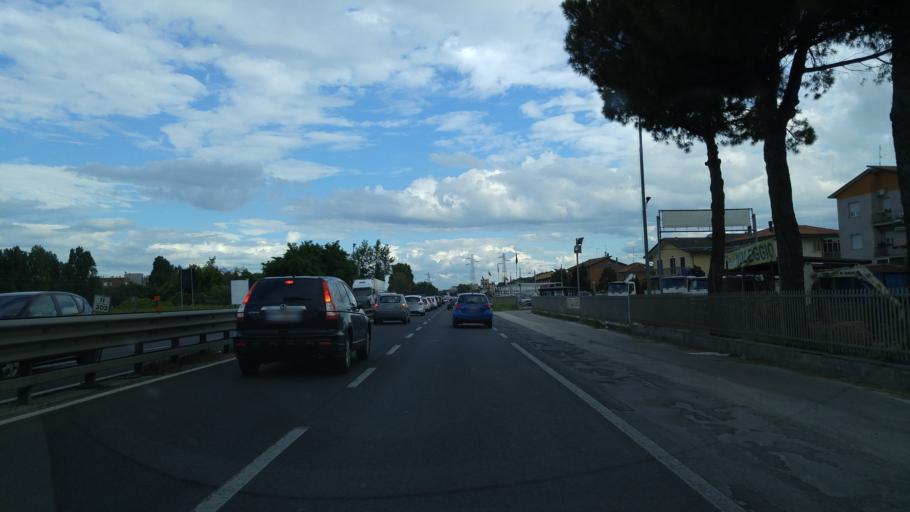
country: IT
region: Emilia-Romagna
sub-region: Provincia di Rimini
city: Rimini
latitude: 44.0537
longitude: 12.5448
